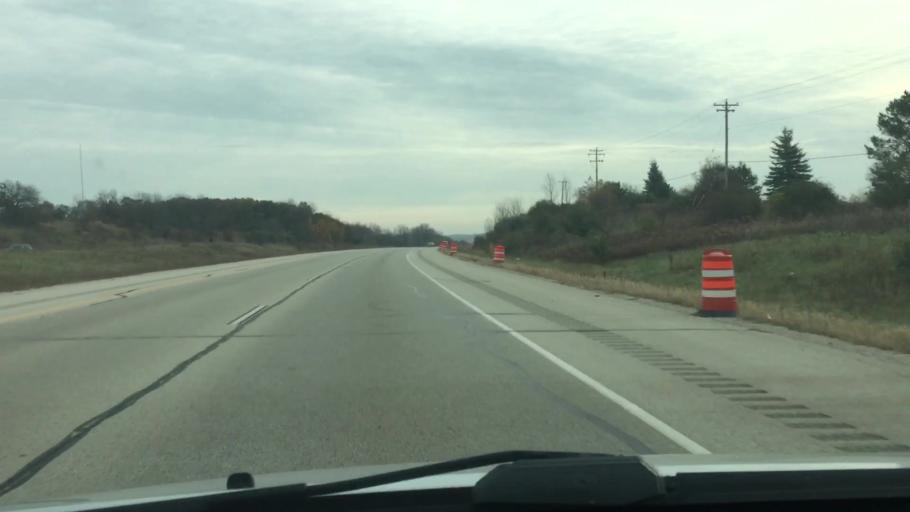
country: US
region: Wisconsin
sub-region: Waukesha County
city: Muskego
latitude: 42.9274
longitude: -88.1829
